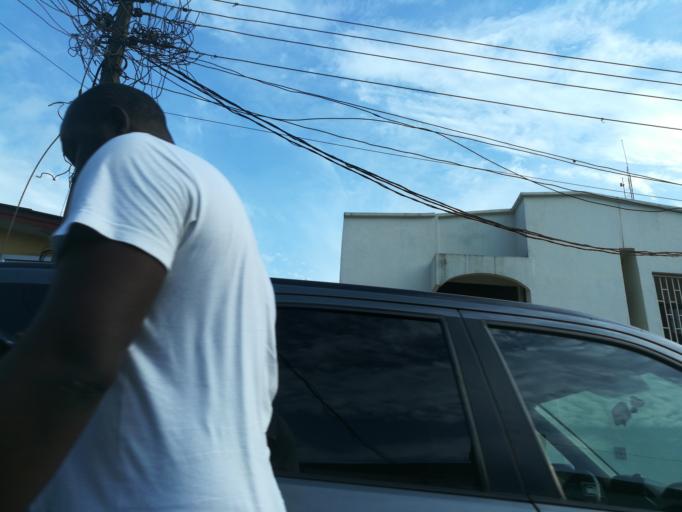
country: NG
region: Lagos
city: Ikeja
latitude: 6.5944
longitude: 3.3464
